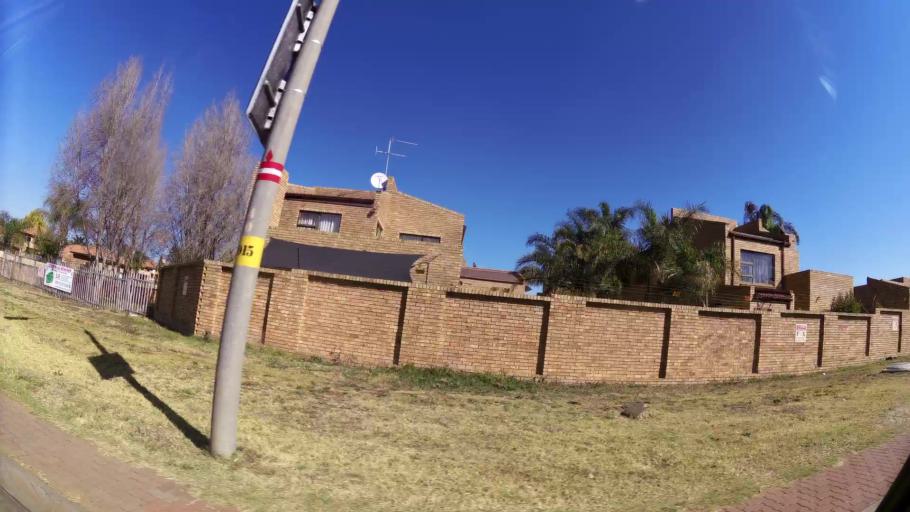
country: ZA
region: Gauteng
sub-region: Ekurhuleni Metropolitan Municipality
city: Germiston
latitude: -26.2963
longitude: 28.0926
